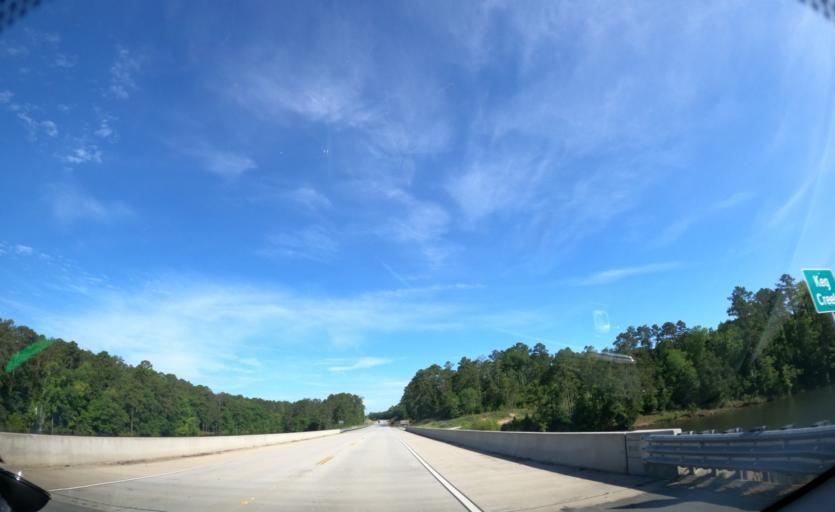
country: US
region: Georgia
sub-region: Columbia County
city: Appling
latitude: 33.6418
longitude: -82.3077
